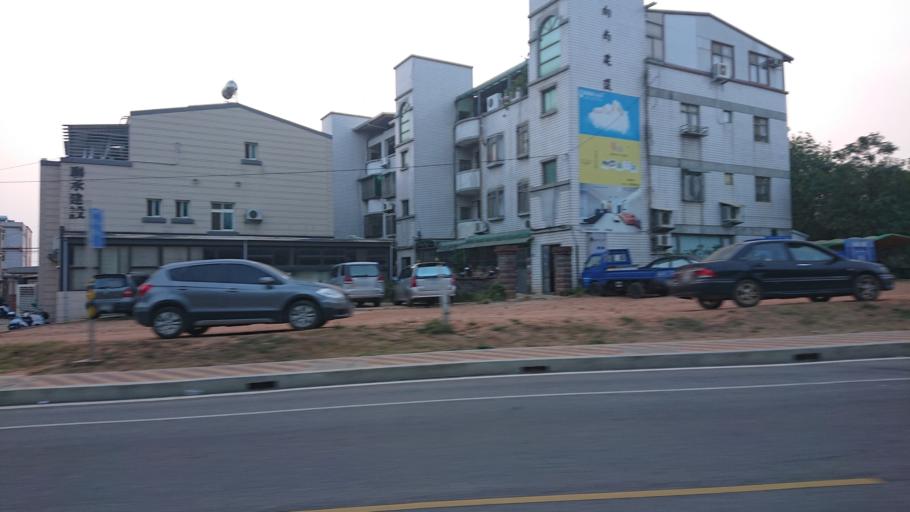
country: TW
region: Fukien
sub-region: Kinmen
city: Jincheng
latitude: 24.4423
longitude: 118.3203
